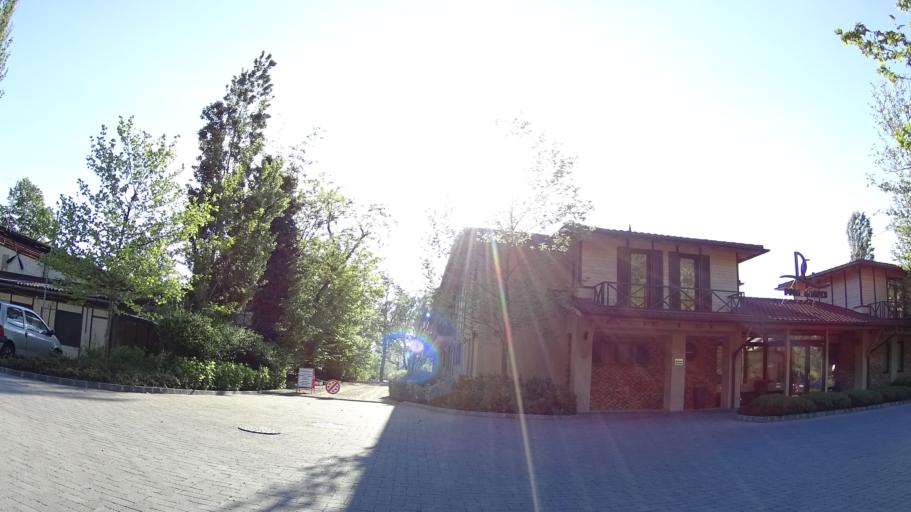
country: HU
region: Budapest
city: Budapest XX. keruelet
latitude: 47.4332
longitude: 19.0909
